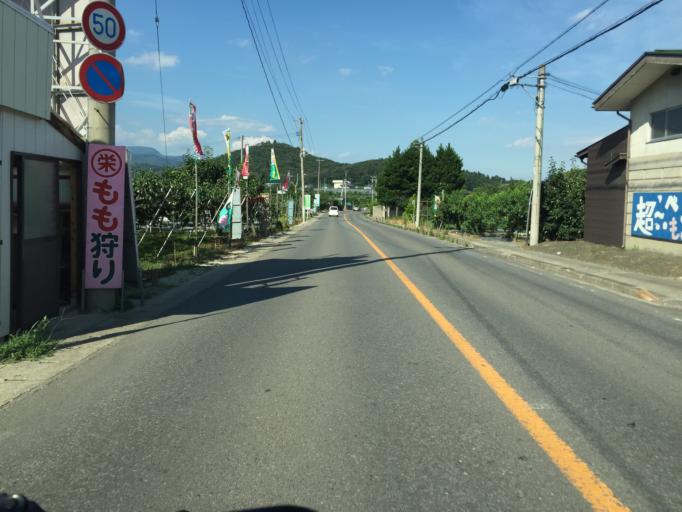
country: JP
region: Fukushima
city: Fukushima-shi
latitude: 37.8120
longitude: 140.4197
